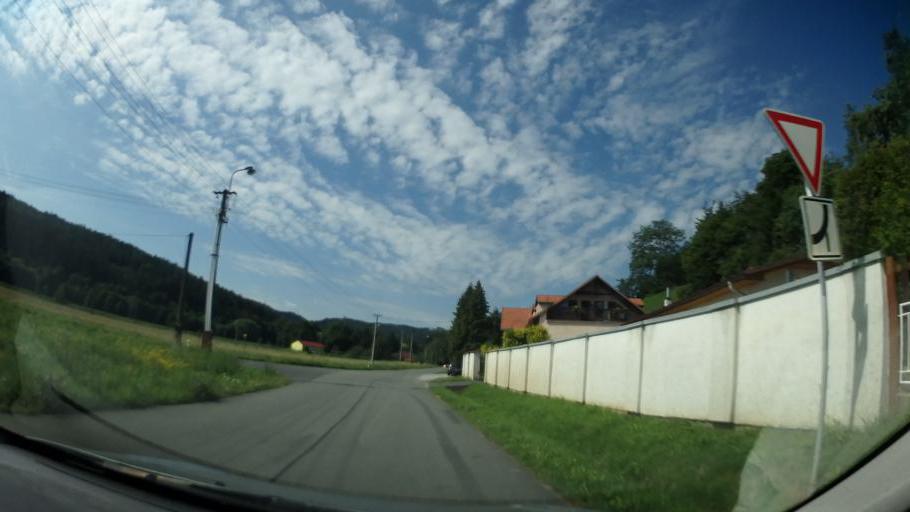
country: CZ
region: Olomoucky
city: Zabreh
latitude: 49.8713
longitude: 16.8452
